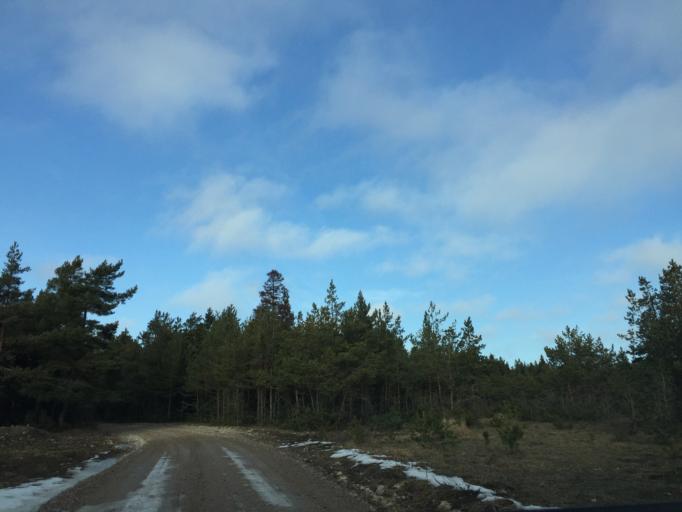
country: EE
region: Saare
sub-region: Kuressaare linn
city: Kuressaare
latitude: 58.4812
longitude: 21.9476
